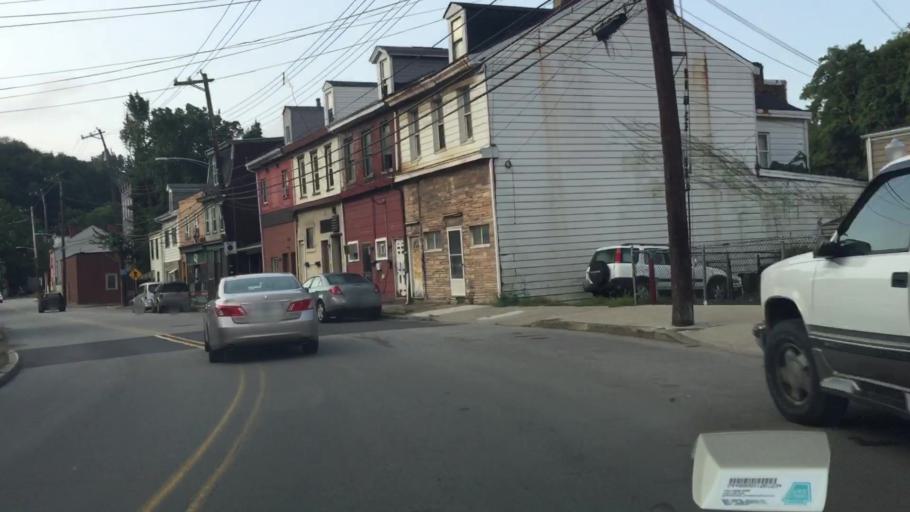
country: US
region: Pennsylvania
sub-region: Allegheny County
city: Millvale
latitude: 40.4863
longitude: -79.9727
